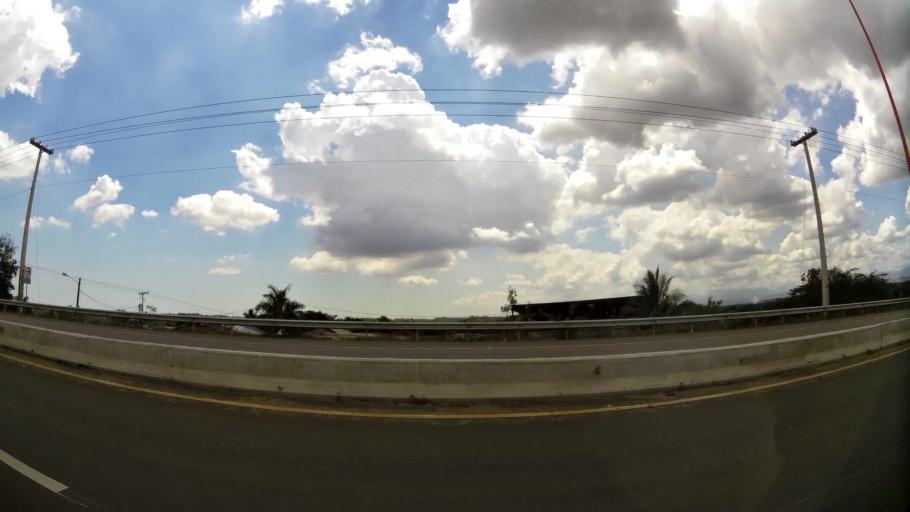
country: DO
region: Nacional
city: Santo Domingo
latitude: 18.5559
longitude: -69.9763
